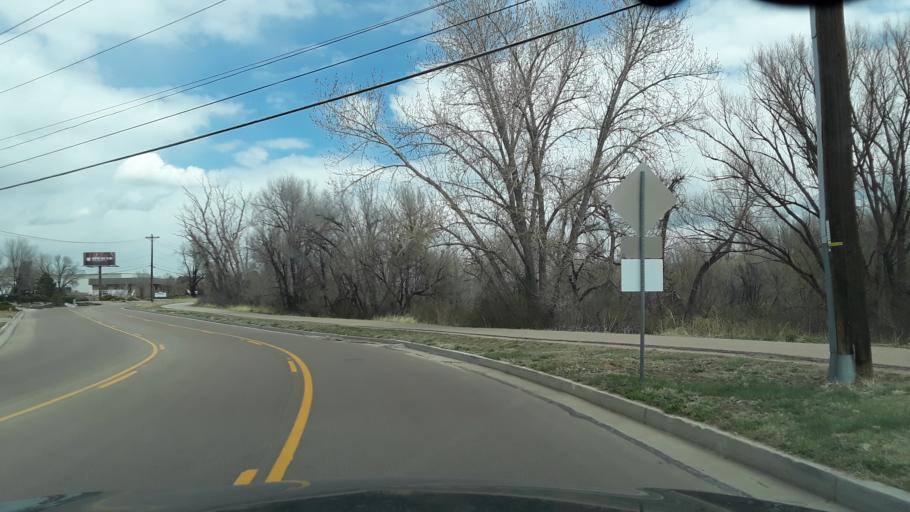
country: US
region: Colorado
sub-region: El Paso County
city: Colorado Springs
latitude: 38.8900
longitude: -104.8252
